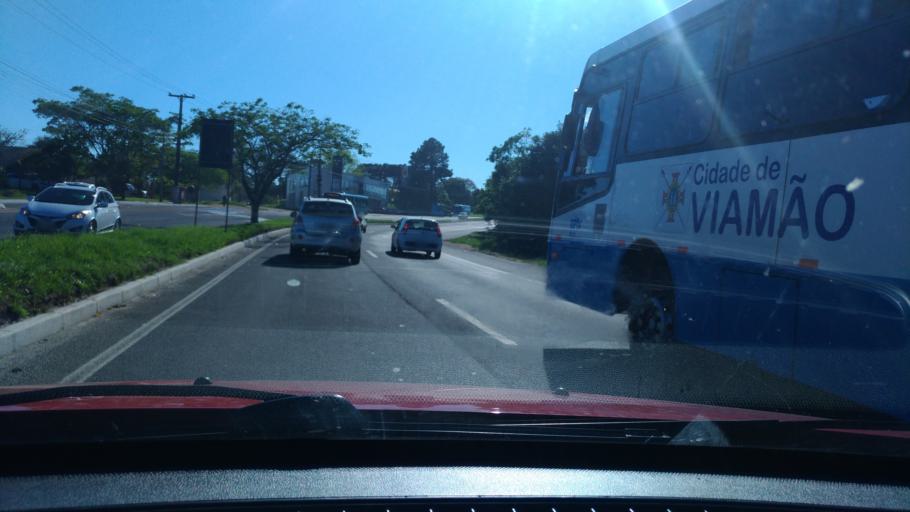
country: BR
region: Rio Grande do Sul
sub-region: Viamao
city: Viamao
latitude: -30.0935
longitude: -51.0766
